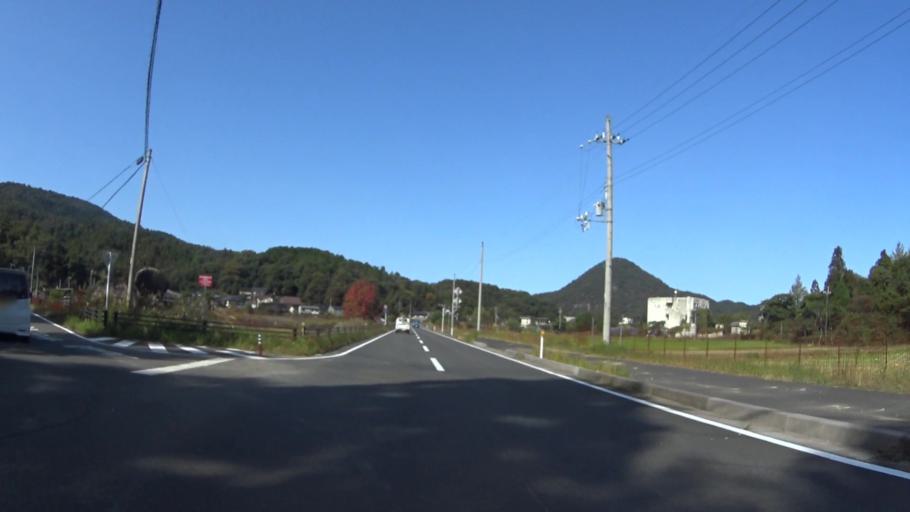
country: JP
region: Hyogo
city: Toyooka
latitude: 35.6256
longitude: 134.8882
